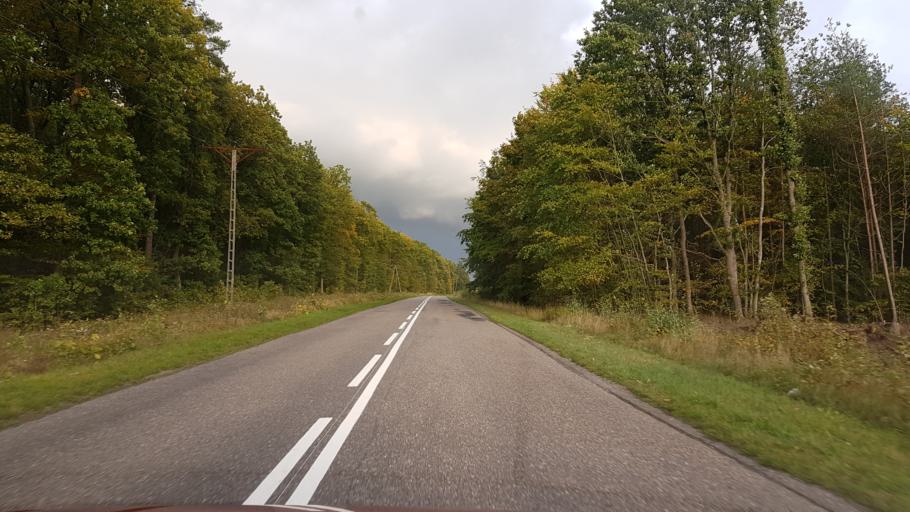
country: PL
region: West Pomeranian Voivodeship
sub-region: Powiat walecki
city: Tuczno
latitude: 53.1751
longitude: 16.3280
